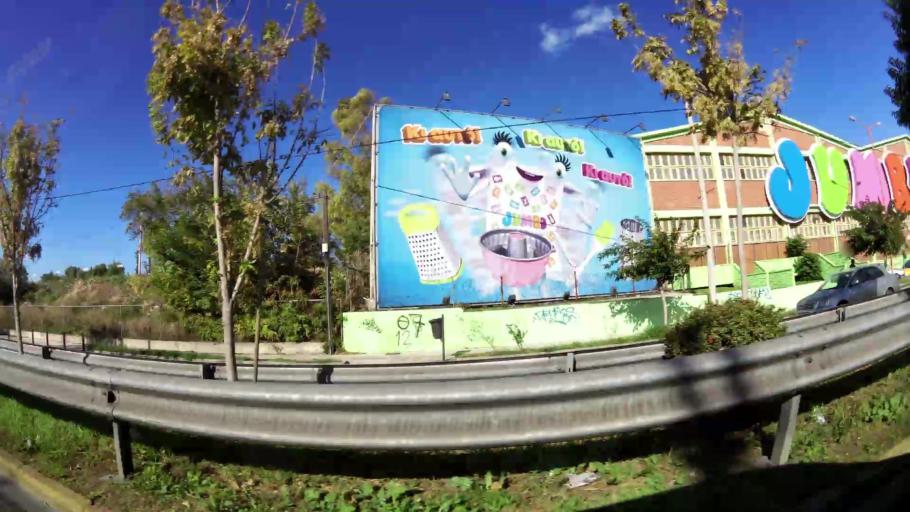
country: GR
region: Attica
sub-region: Nomarchia Athinas
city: Aigaleo
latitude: 37.9794
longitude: 23.6702
